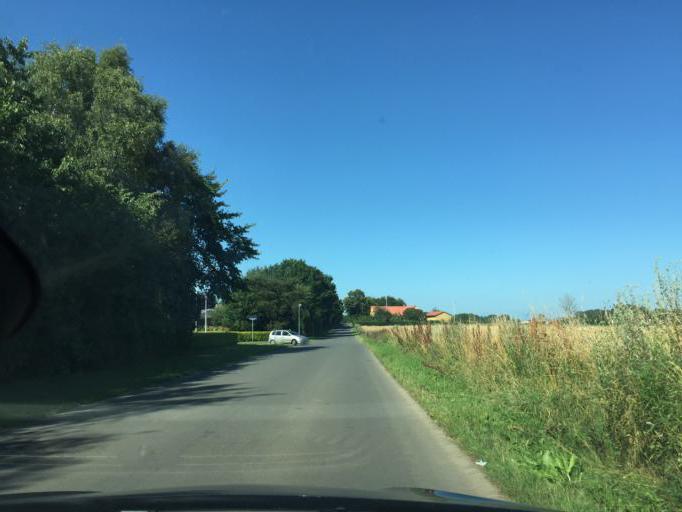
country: DK
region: South Denmark
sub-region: Nordfyns Kommune
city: Sonderso
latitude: 55.4917
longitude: 10.2632
